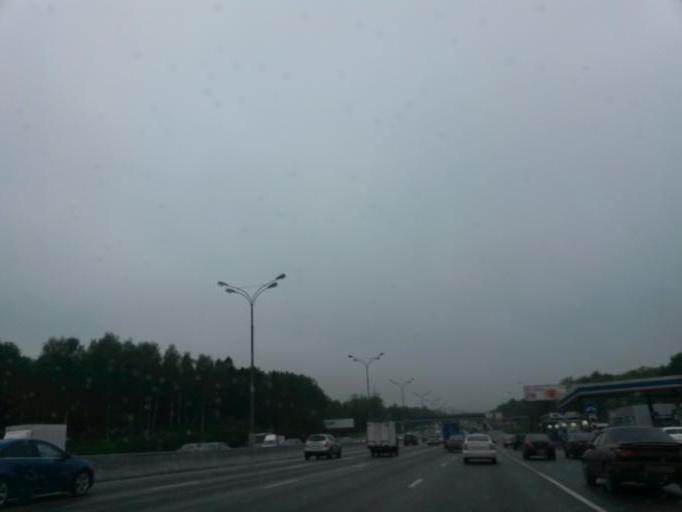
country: RU
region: Moscow
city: Yasenevo
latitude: 55.5903
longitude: 37.5346
